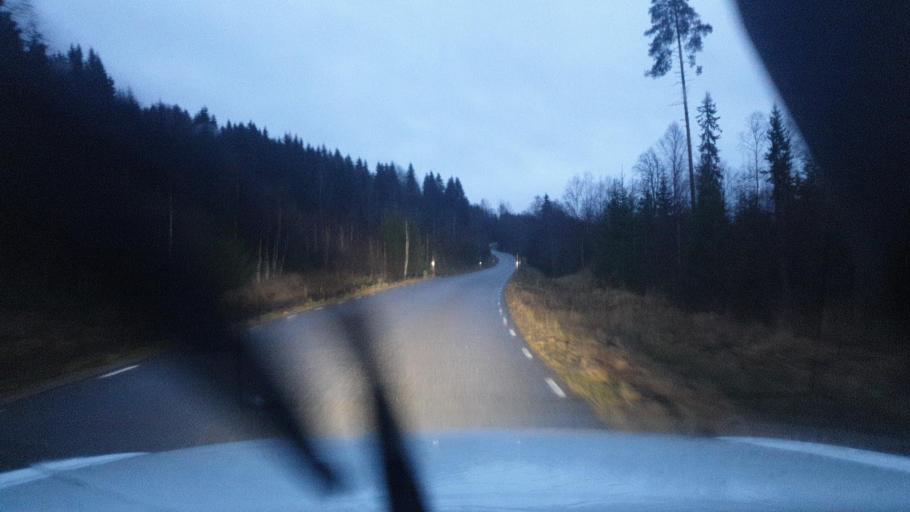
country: SE
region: Vaermland
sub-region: Arvika Kommun
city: Arvika
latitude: 60.0161
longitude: 12.6578
